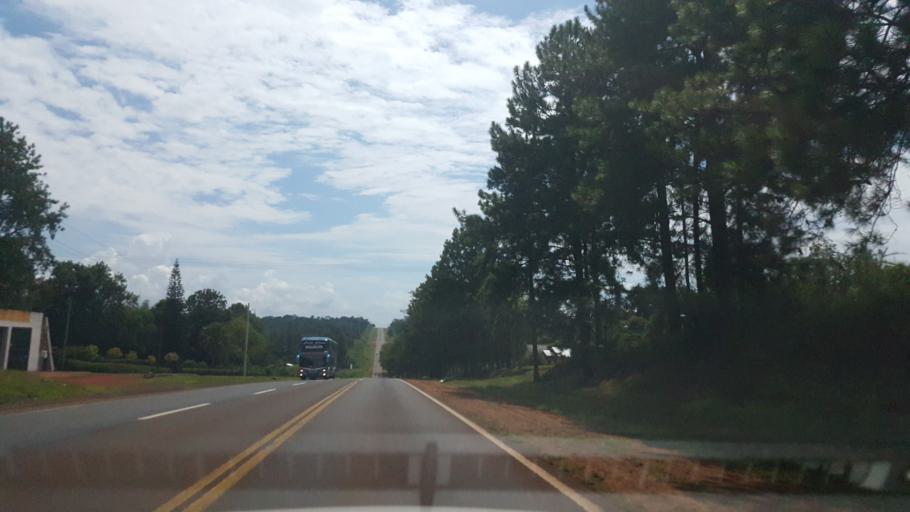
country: AR
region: Misiones
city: Capiovi
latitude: -26.9002
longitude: -55.0596
